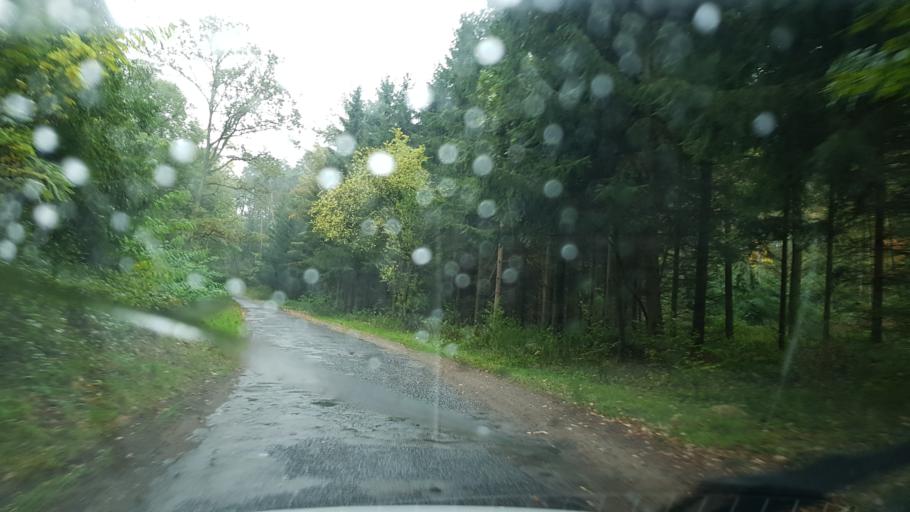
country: PL
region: West Pomeranian Voivodeship
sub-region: Powiat mysliborski
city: Barlinek
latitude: 53.0222
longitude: 15.2212
